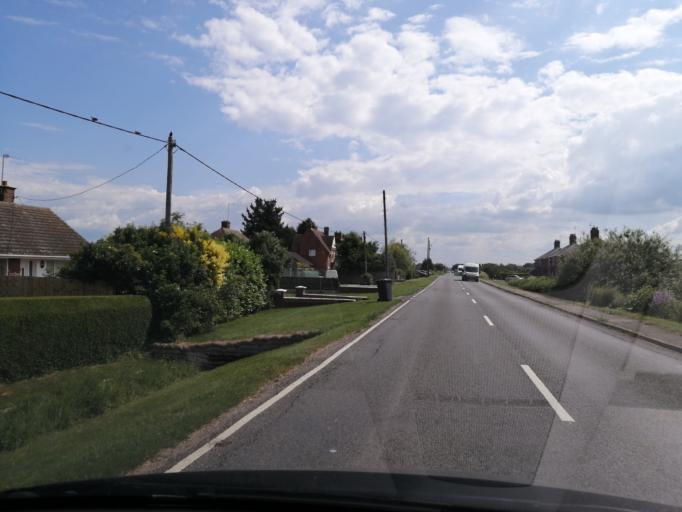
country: GB
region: England
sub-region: Cambridgeshire
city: Ramsey
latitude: 52.4860
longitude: -0.1497
